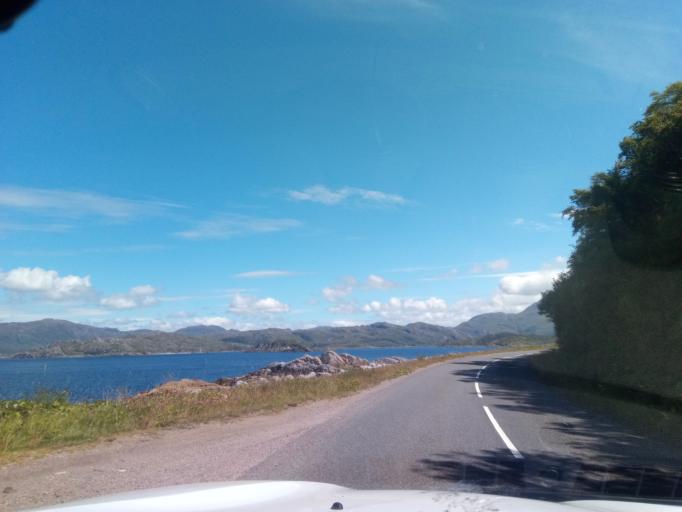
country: GB
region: Scotland
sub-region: Argyll and Bute
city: Isle Of Mull
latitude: 56.8374
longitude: -5.8087
